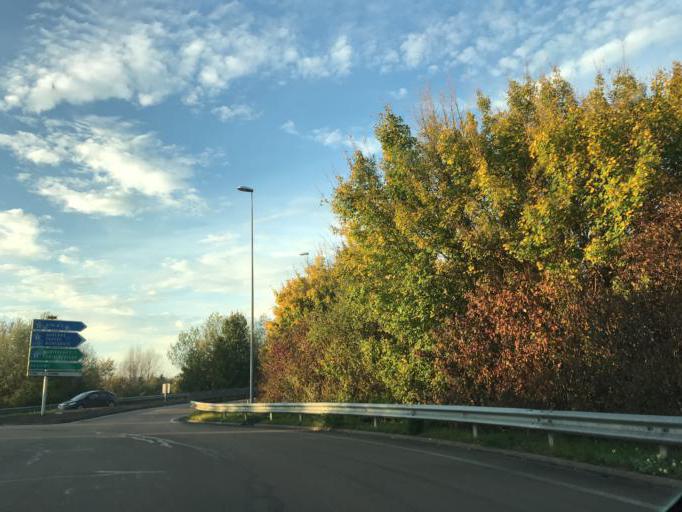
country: FR
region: Bourgogne
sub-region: Departement de l'Yonne
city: Saint-Martin-du-Tertre
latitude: 48.2319
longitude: 3.2641
